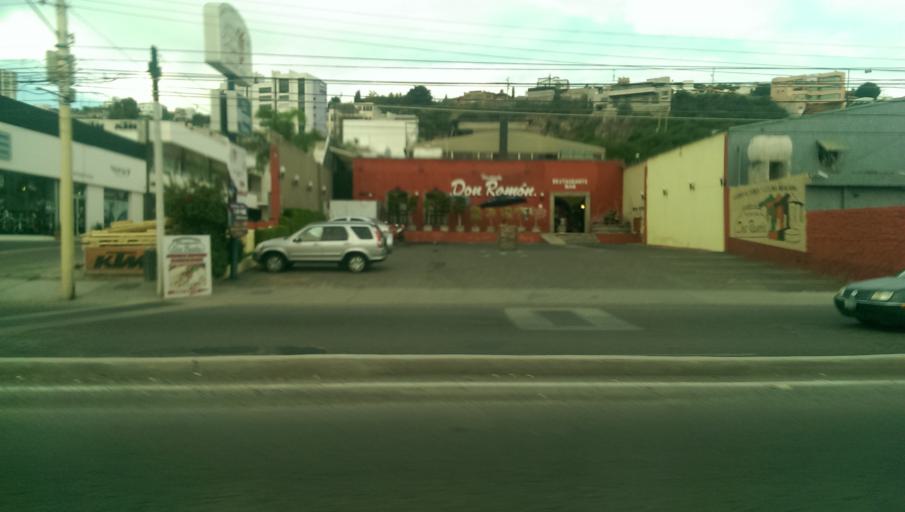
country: MX
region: Queretaro
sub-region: Queretaro
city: Santiago de Queretaro
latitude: 20.5916
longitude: -100.3670
